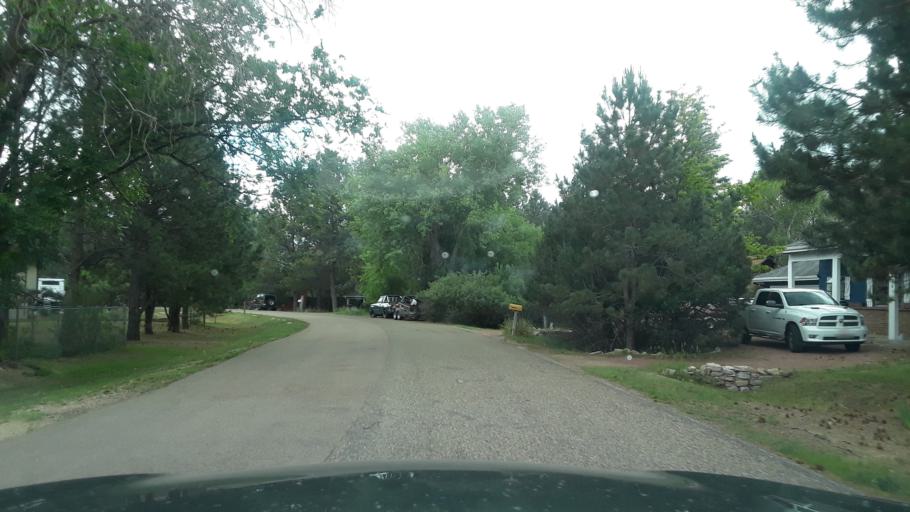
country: US
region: Colorado
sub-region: El Paso County
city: Air Force Academy
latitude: 38.9467
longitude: -104.8259
